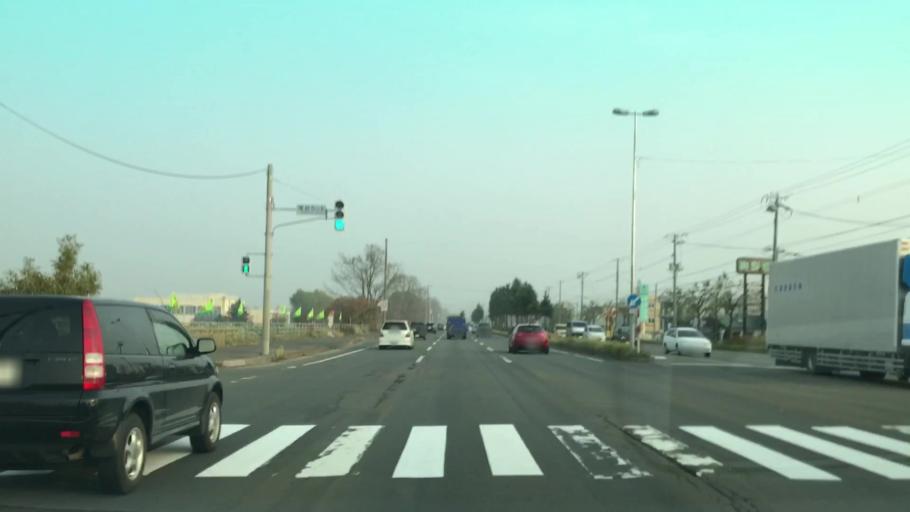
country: JP
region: Hokkaido
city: Sapporo
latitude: 43.1502
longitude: 141.3509
